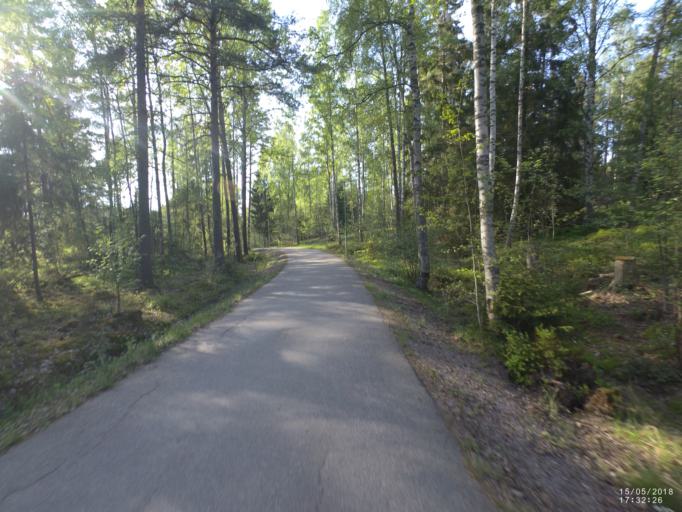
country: SE
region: Soedermanland
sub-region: Nykopings Kommun
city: Nykoping
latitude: 58.7355
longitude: 17.0126
